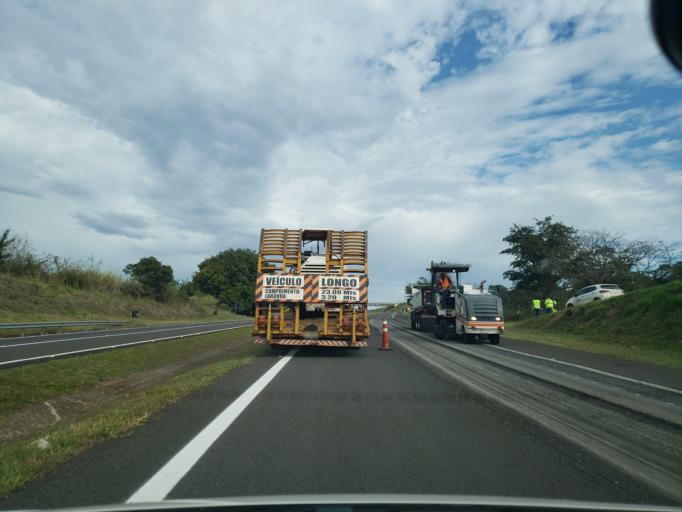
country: BR
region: Sao Paulo
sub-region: Dois Corregos
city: Dois Corregos
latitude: -22.2489
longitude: -48.3546
